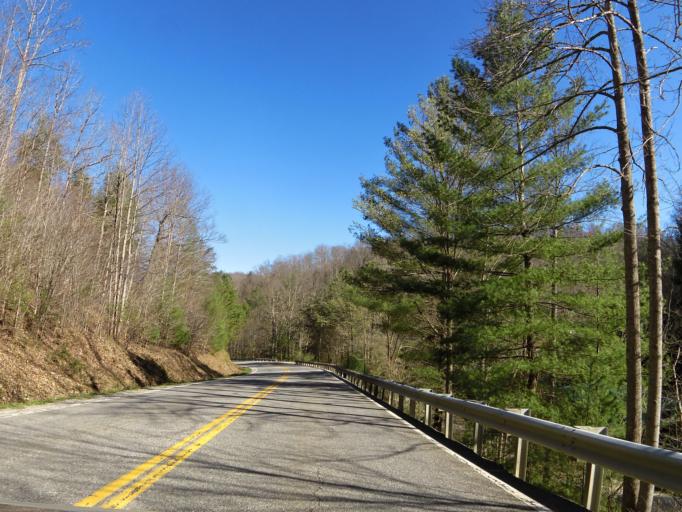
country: US
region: Tennessee
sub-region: Scott County
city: Oneida
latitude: 36.4784
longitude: -84.4978
